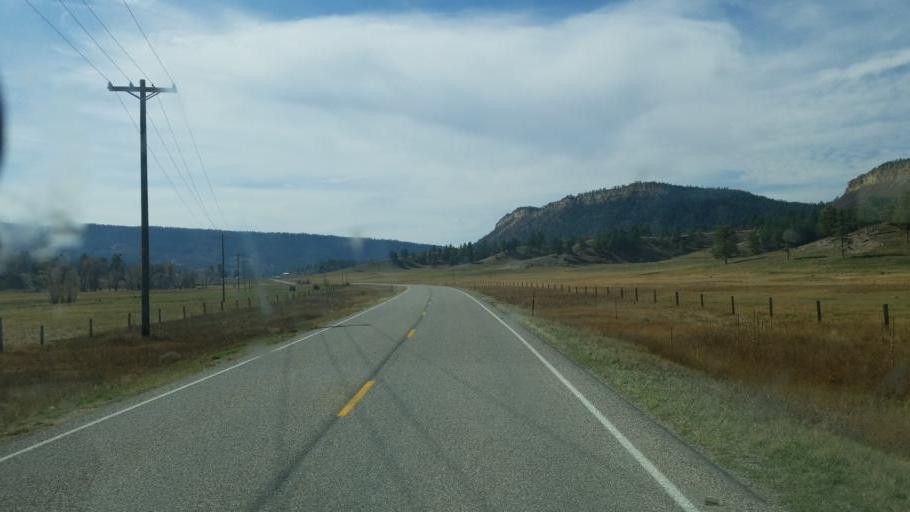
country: US
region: New Mexico
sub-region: Rio Arriba County
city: Dulce
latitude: 37.0614
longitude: -106.8357
